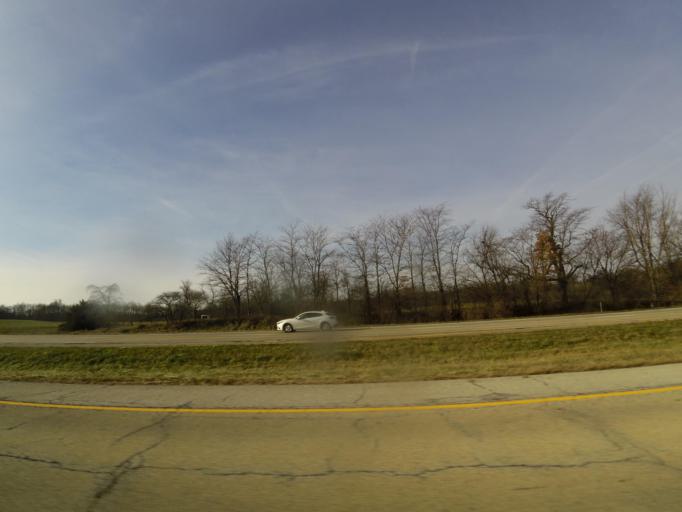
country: US
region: Illinois
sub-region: De Witt County
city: Clinton
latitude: 40.0962
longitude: -88.9655
